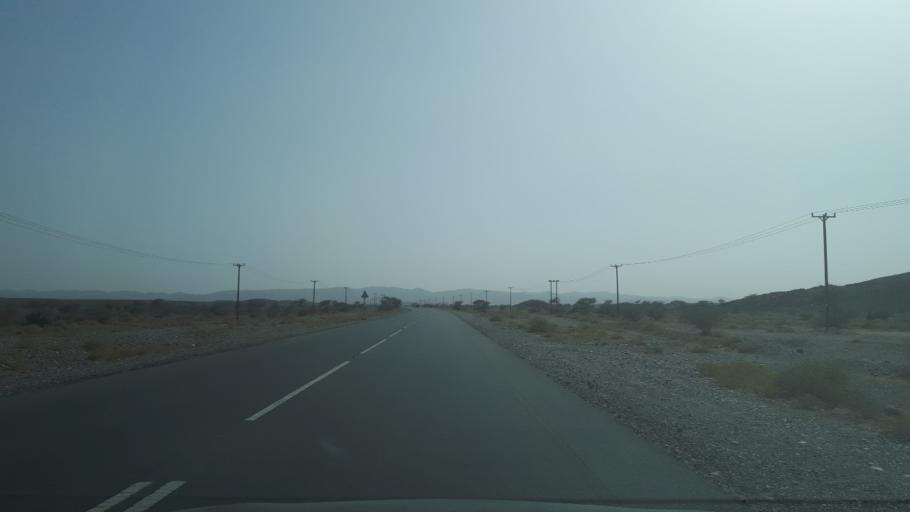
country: OM
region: Az Zahirah
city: `Ibri
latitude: 23.1049
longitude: 56.8705
